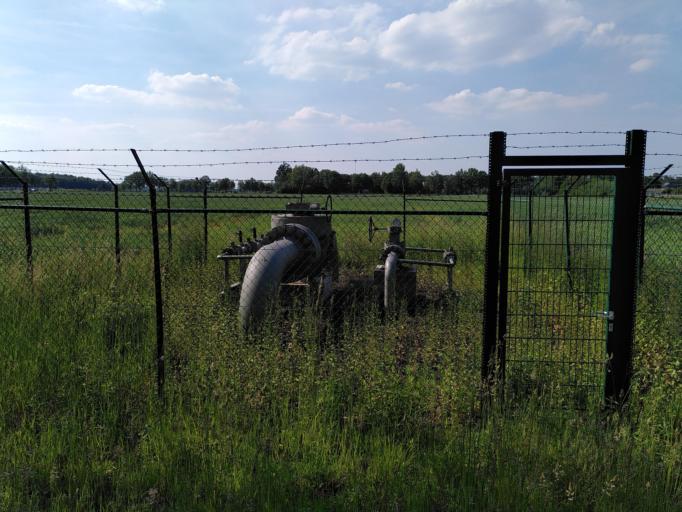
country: DE
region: North Rhine-Westphalia
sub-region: Regierungsbezirk Munster
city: Gronau
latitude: 52.1689
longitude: 6.9974
